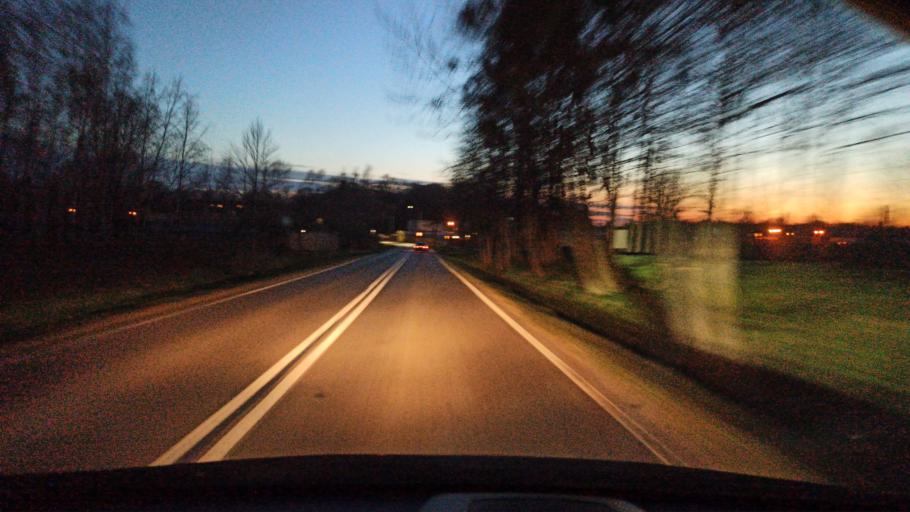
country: PL
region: Warmian-Masurian Voivodeship
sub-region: Powiat elblaski
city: Gronowo Gorne
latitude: 54.1607
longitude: 19.4571
